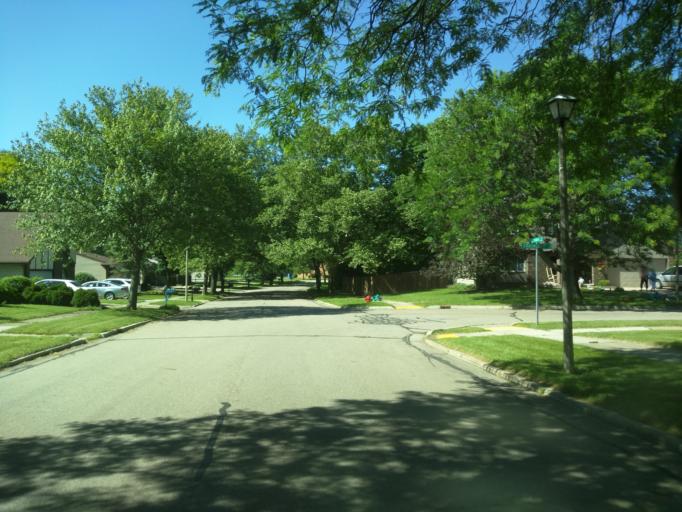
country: US
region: Michigan
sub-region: Ingham County
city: Edgemont Park
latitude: 42.7596
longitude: -84.5935
